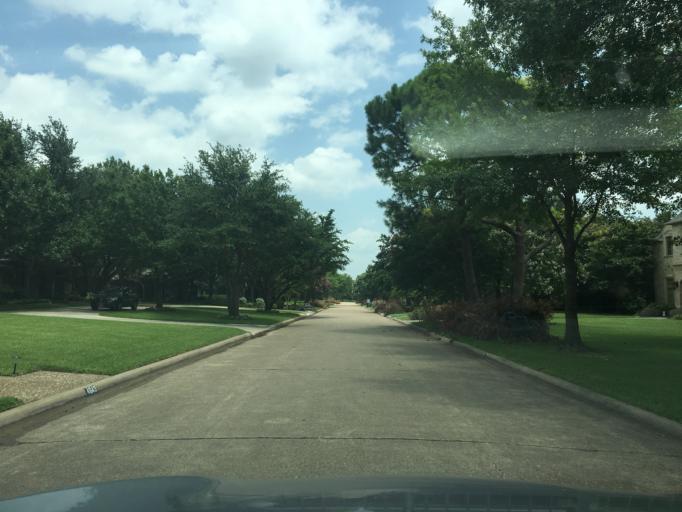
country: US
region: Texas
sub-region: Dallas County
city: University Park
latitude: 32.8986
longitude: -96.8281
